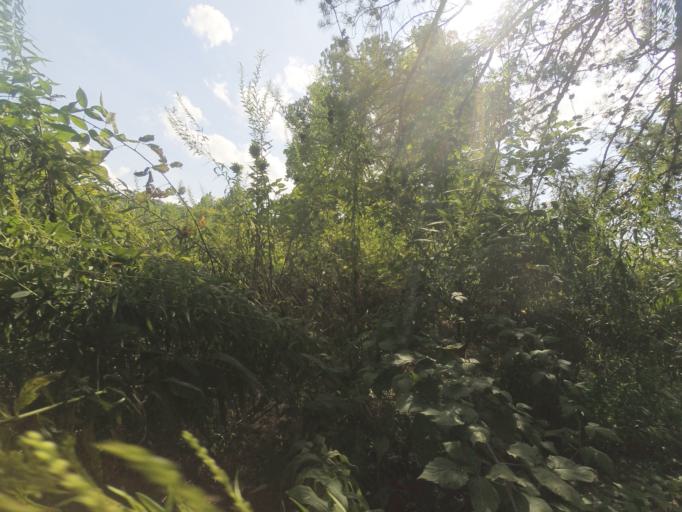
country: US
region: Ohio
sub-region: Lawrence County
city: Burlington
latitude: 38.3839
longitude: -82.5143
